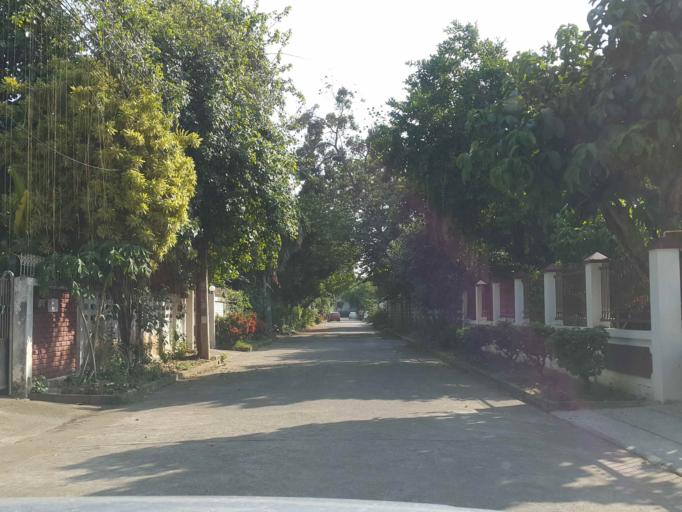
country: TH
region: Chiang Mai
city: Chiang Mai
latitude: 18.7681
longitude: 98.9961
